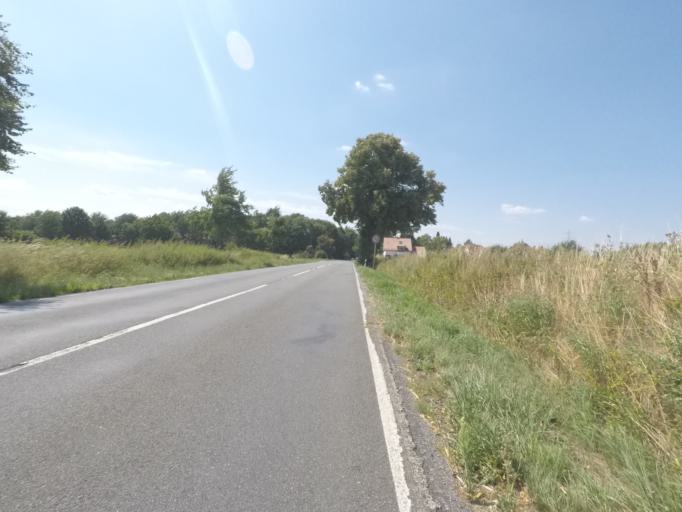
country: DE
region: North Rhine-Westphalia
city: Enger
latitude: 52.1048
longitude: 8.5915
